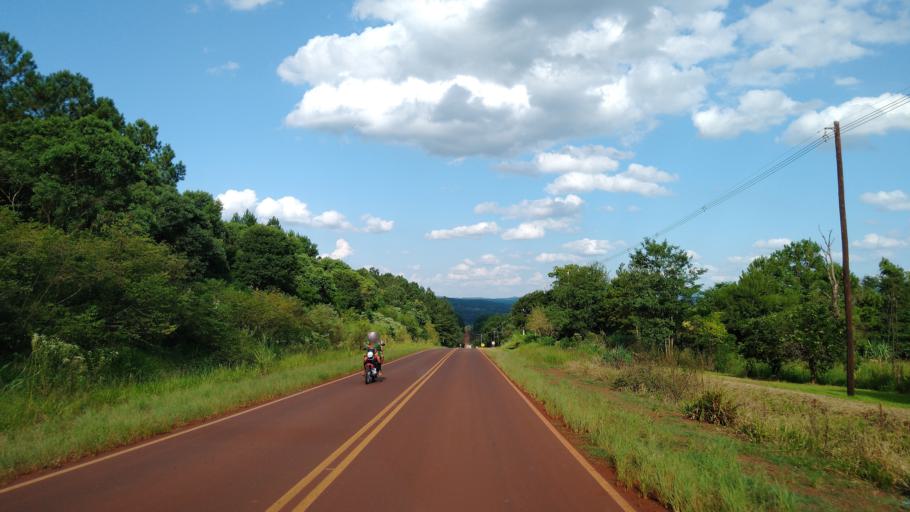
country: AR
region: Misiones
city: Puerto Piray
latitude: -26.4781
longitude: -54.6757
